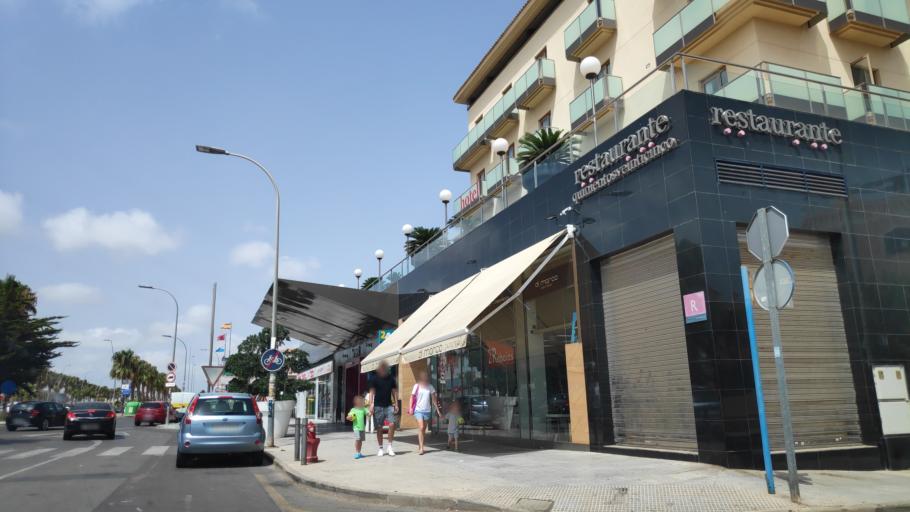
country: ES
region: Murcia
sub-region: Murcia
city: Los Alcazares
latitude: 37.7542
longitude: -0.8466
